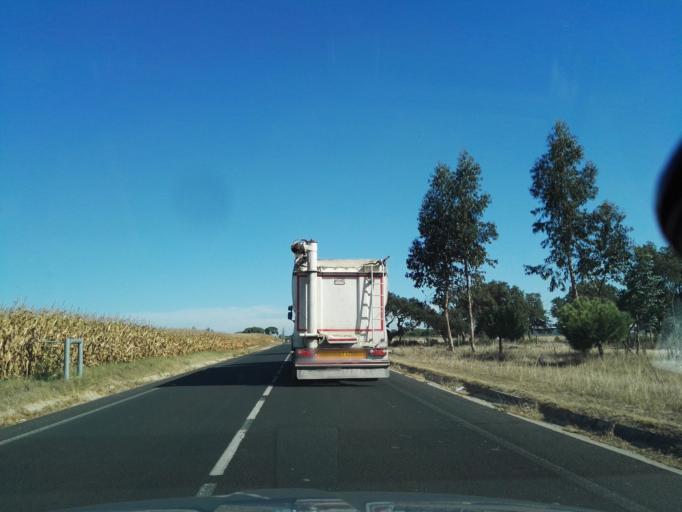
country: PT
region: Santarem
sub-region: Benavente
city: Benavente
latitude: 38.9480
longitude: -8.8196
